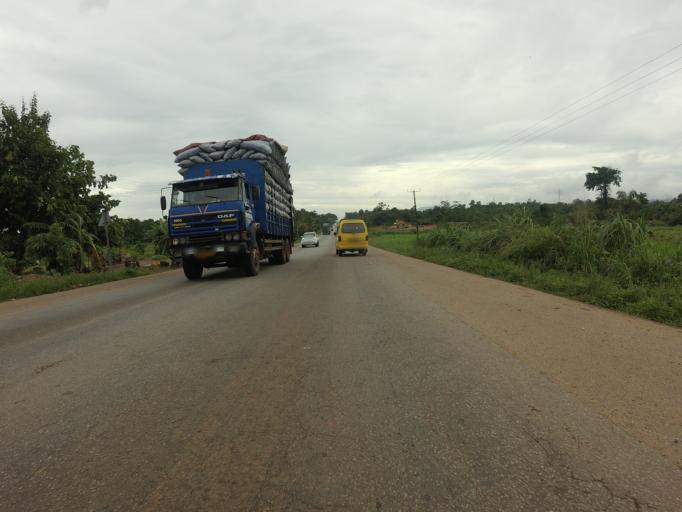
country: GH
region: Eastern
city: Nkawkaw
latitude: 6.4804
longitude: -0.6621
